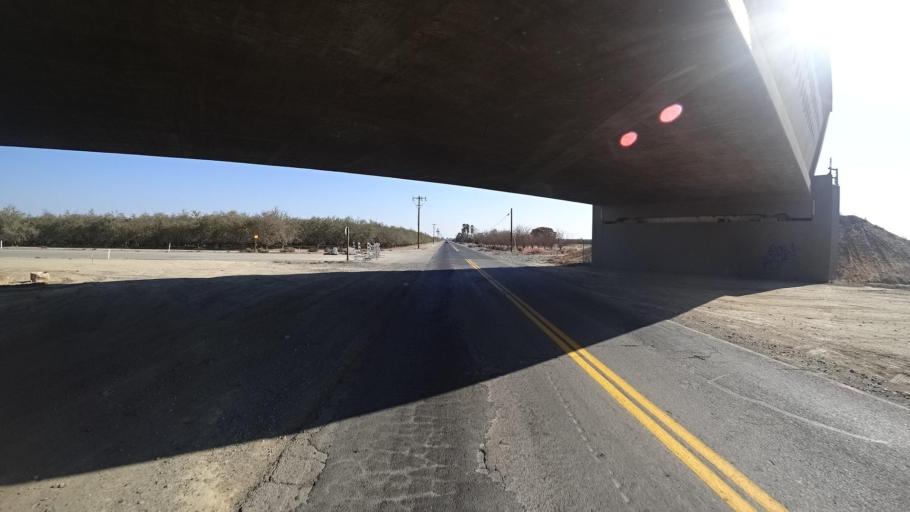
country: US
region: California
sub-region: Kern County
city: Delano
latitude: 35.7177
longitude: -119.3606
